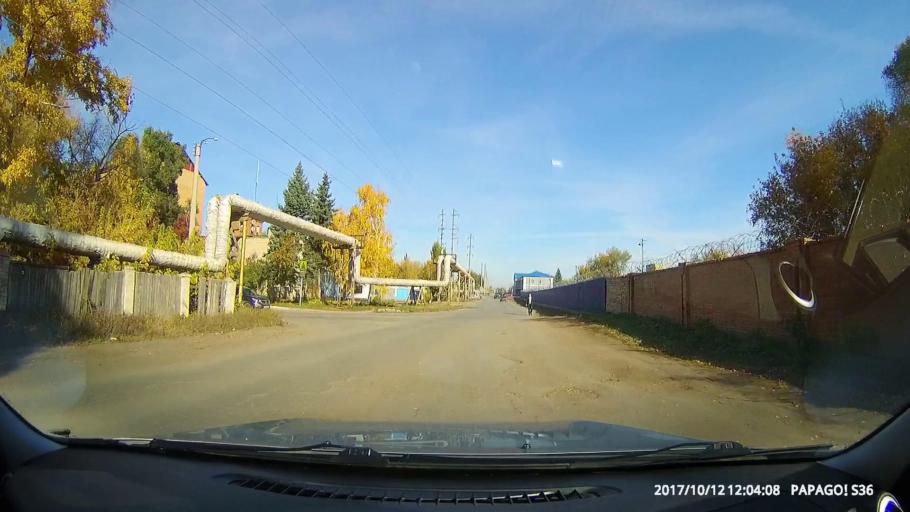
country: RU
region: Samara
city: Chapayevsk
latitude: 52.9773
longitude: 49.7174
